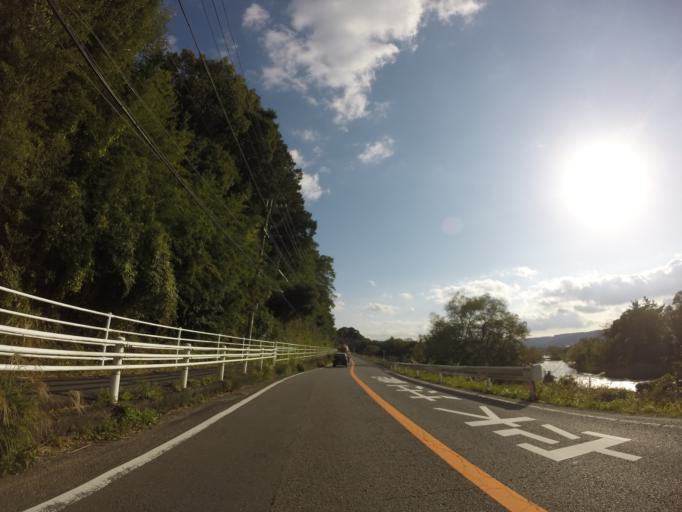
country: JP
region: Shizuoka
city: Kanaya
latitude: 34.8485
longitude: 138.1435
